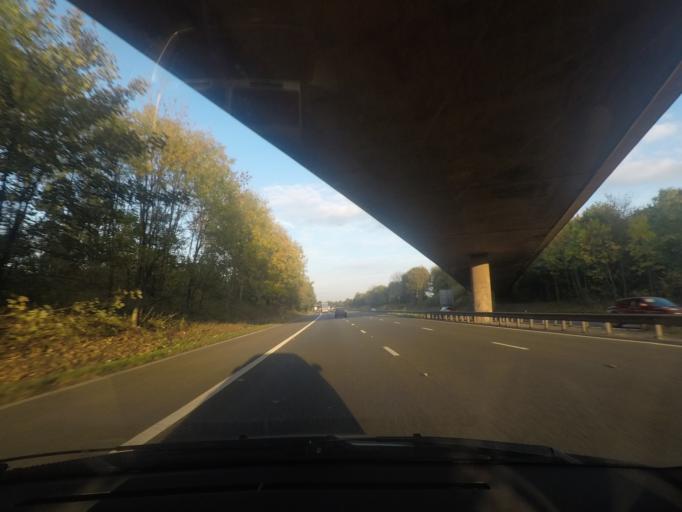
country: GB
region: England
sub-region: North Lincolnshire
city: Scawby
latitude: 53.5501
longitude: -0.5243
